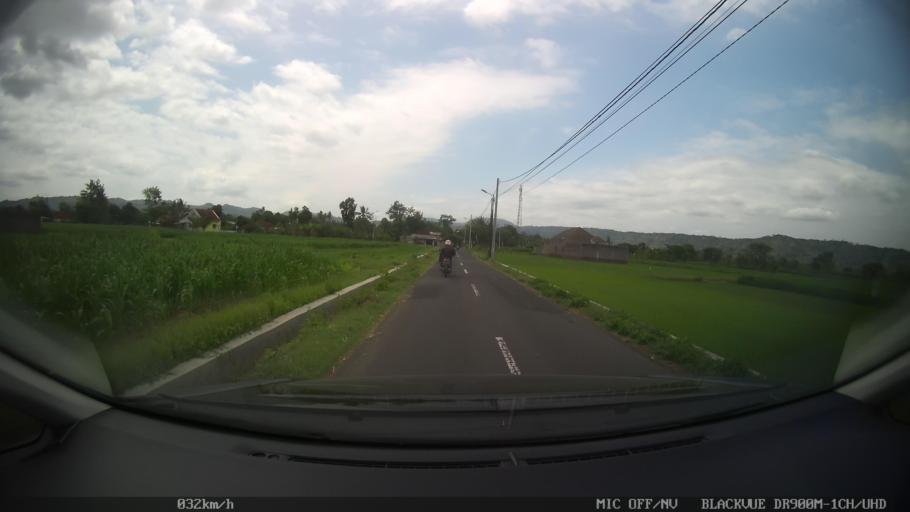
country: ID
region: Central Java
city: Candi Prambanan
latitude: -7.8144
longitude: 110.4759
